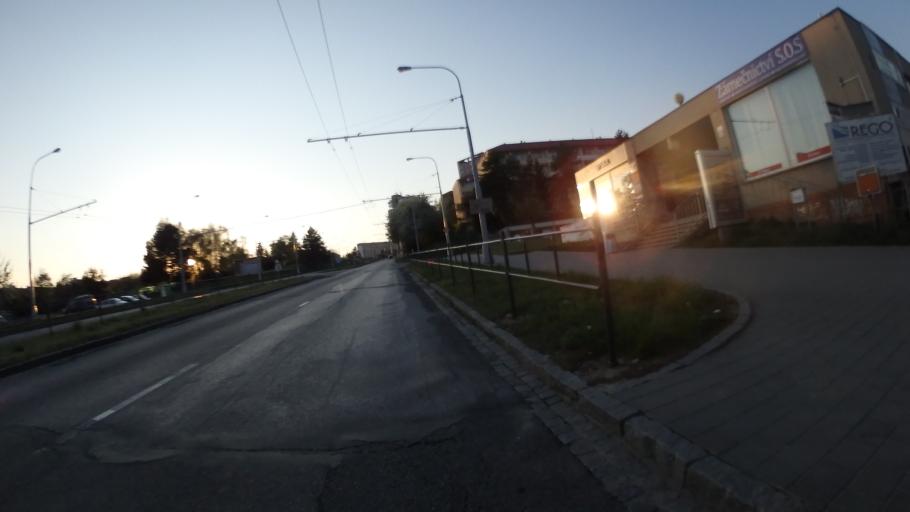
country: CZ
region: South Moravian
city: Ostopovice
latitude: 49.1951
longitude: 16.5396
